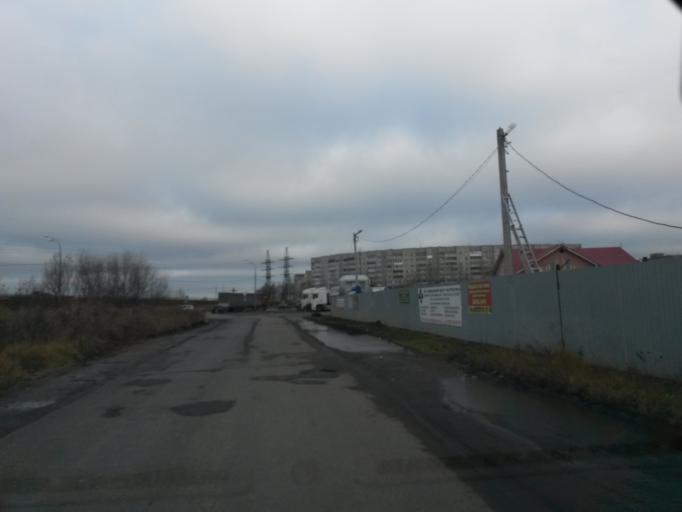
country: RU
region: Jaroslavl
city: Rostov
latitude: 57.2025
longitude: 39.4269
